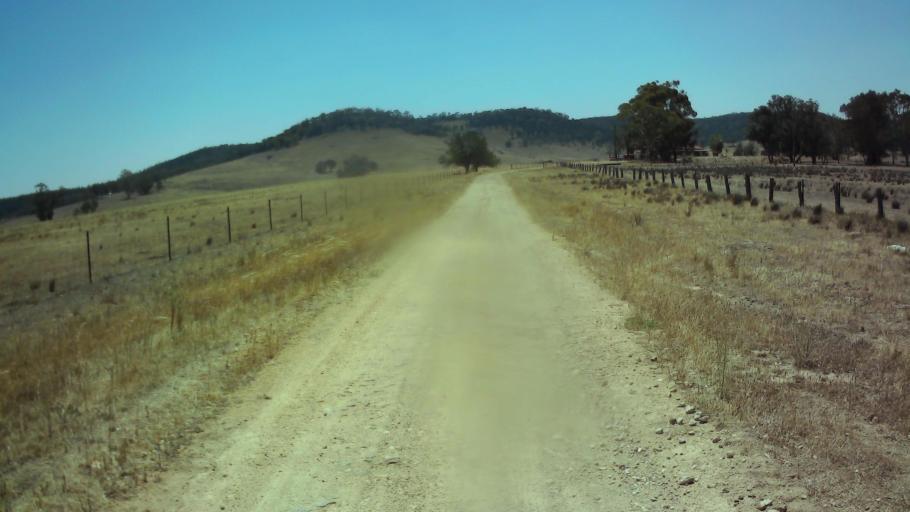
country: AU
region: New South Wales
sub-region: Weddin
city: Grenfell
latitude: -33.9136
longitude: 148.3216
